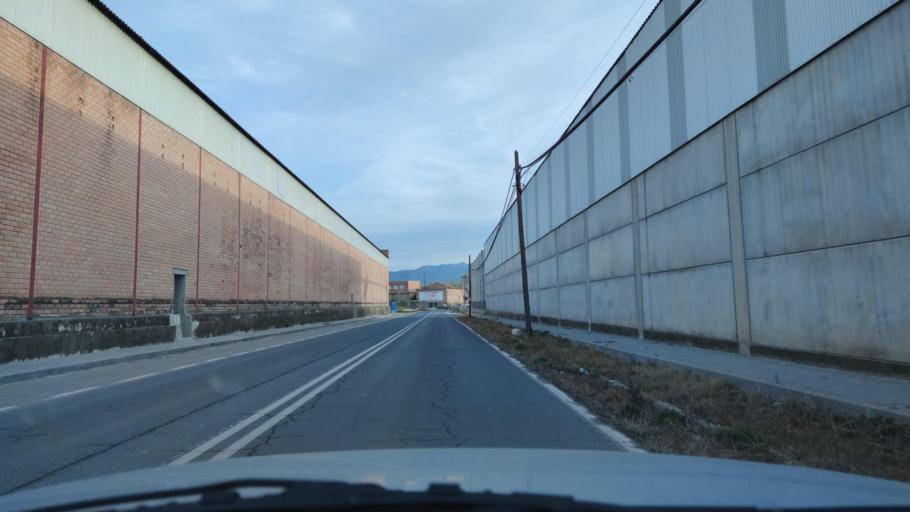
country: ES
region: Catalonia
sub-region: Provincia de Lleida
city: Balaguer
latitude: 41.8009
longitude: 0.8080
